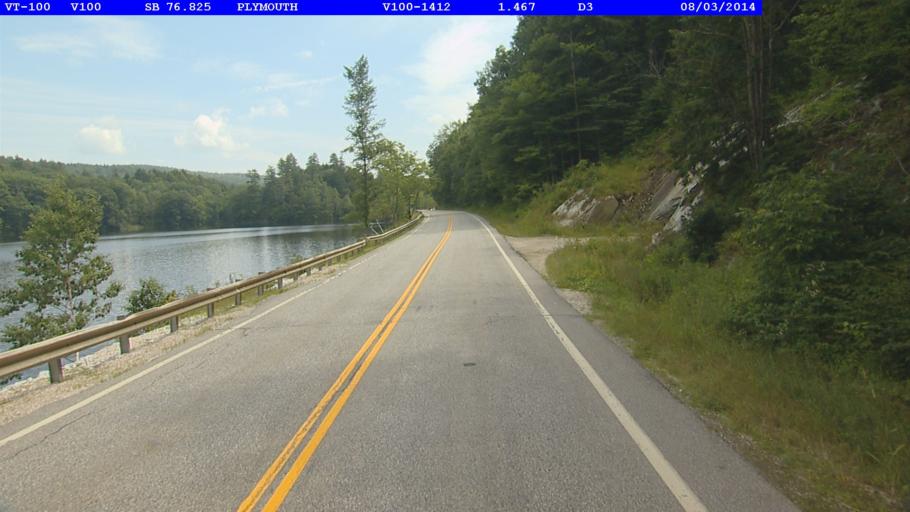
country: US
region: Vermont
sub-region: Windsor County
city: Woodstock
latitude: 43.4836
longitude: -72.7052
